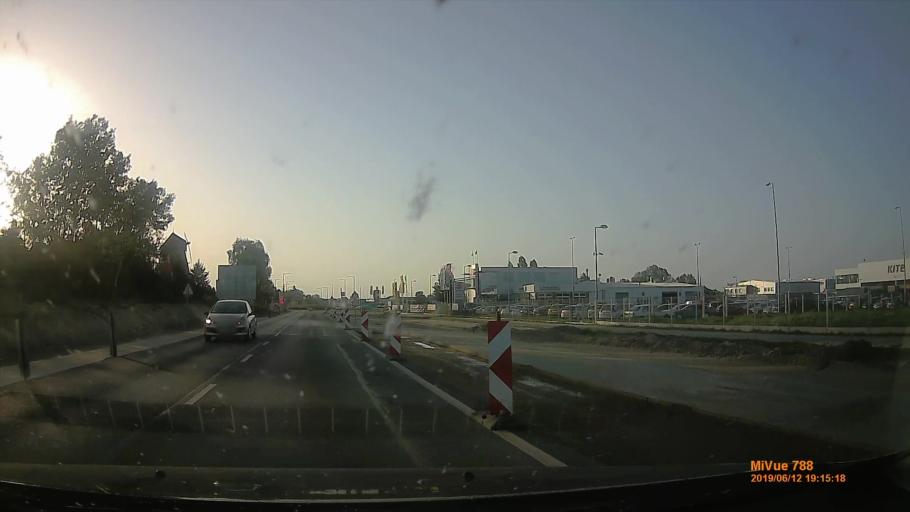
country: HU
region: Bacs-Kiskun
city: Kecskemet
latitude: 46.8799
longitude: 19.7089
